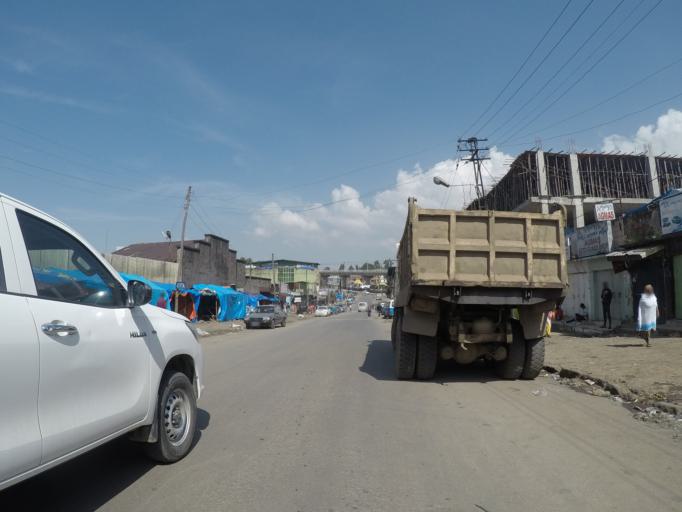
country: ET
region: Adis Abeba
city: Addis Ababa
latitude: 9.0333
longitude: 38.7448
